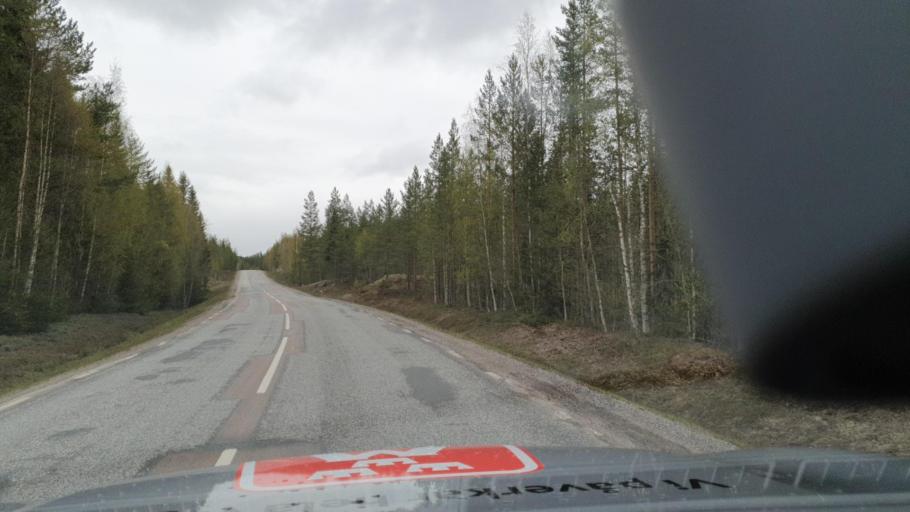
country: SE
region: Vaesternorrland
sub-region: Solleftea Kommun
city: Solleftea
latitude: 63.6692
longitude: 17.2561
